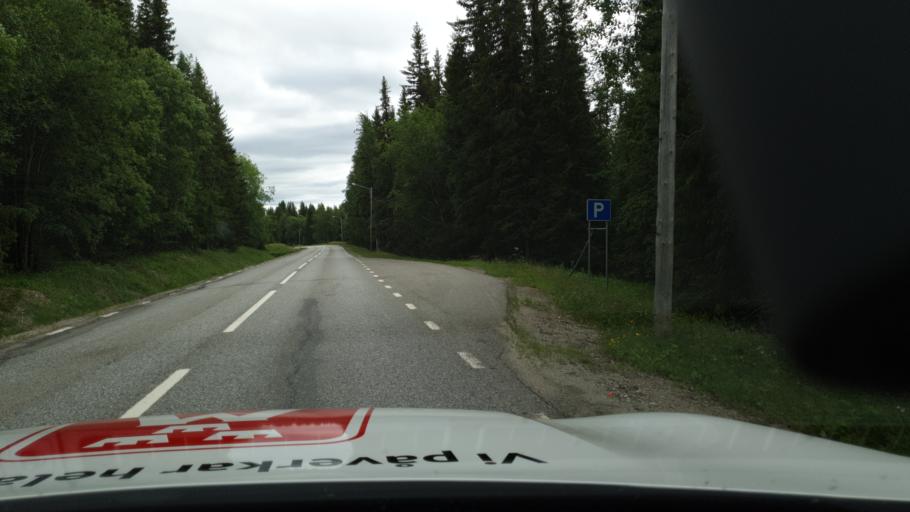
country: SE
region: Vaesterbotten
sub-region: Lycksele Kommun
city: Soderfors
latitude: 64.6508
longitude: 17.8492
